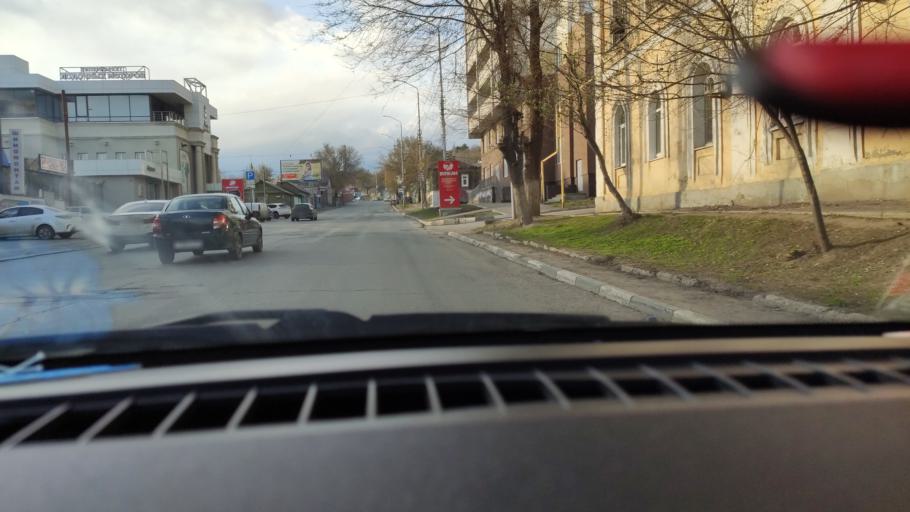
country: RU
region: Saratov
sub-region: Saratovskiy Rayon
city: Saratov
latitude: 51.5387
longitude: 46.0551
